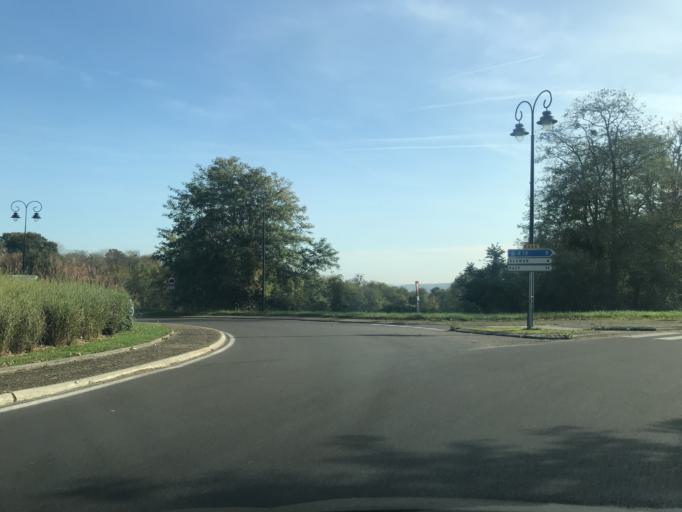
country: FR
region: Haute-Normandie
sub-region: Departement de l'Eure
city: Saint-Just
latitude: 49.0954
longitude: 1.4298
